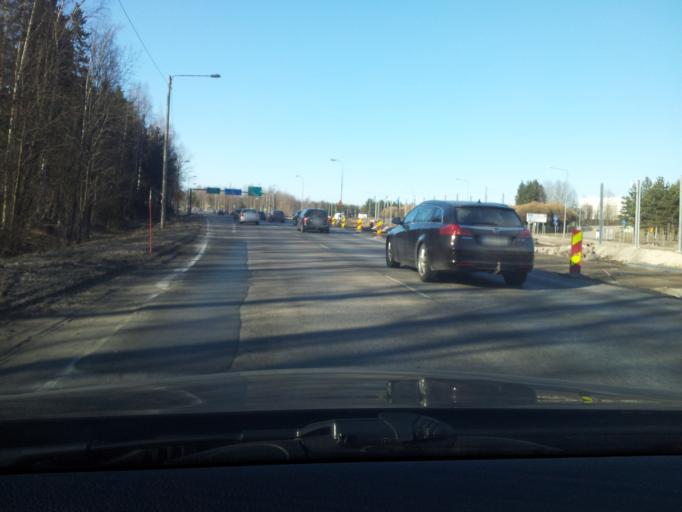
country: FI
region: Uusimaa
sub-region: Helsinki
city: Vantaa
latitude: 60.2341
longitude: 25.0485
